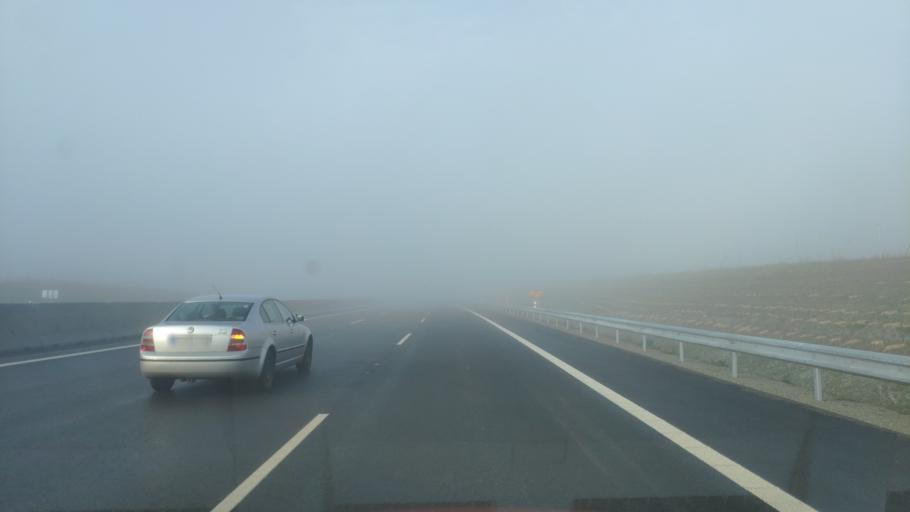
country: SK
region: Kosicky
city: Kosice
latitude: 48.7302
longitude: 21.4071
